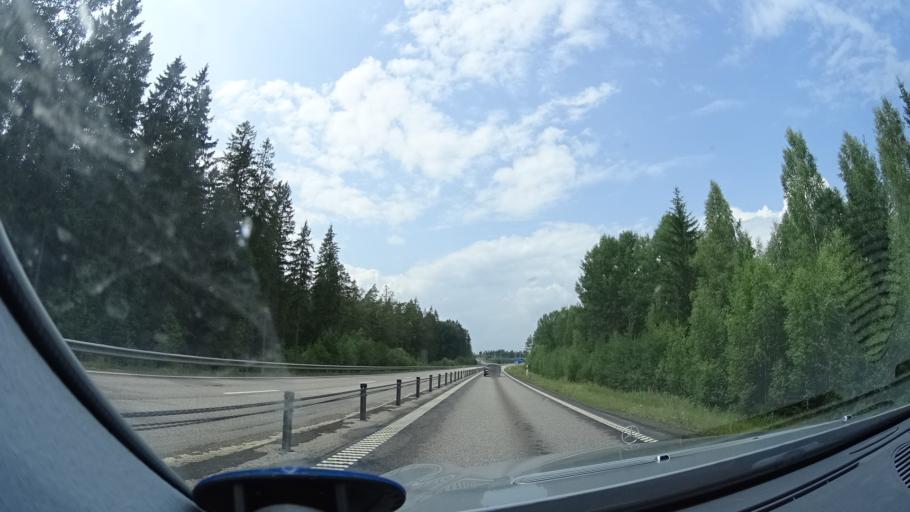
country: SE
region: Kalmar
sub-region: Nybro Kommun
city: Nybro
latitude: 56.7264
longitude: 15.8957
